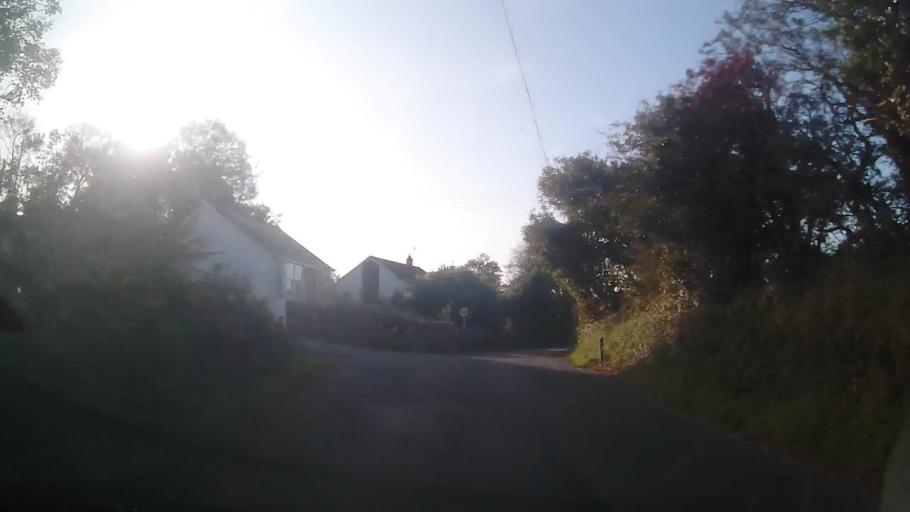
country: GB
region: Wales
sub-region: Pembrokeshire
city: Fishguard
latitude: 51.9903
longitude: -4.9661
